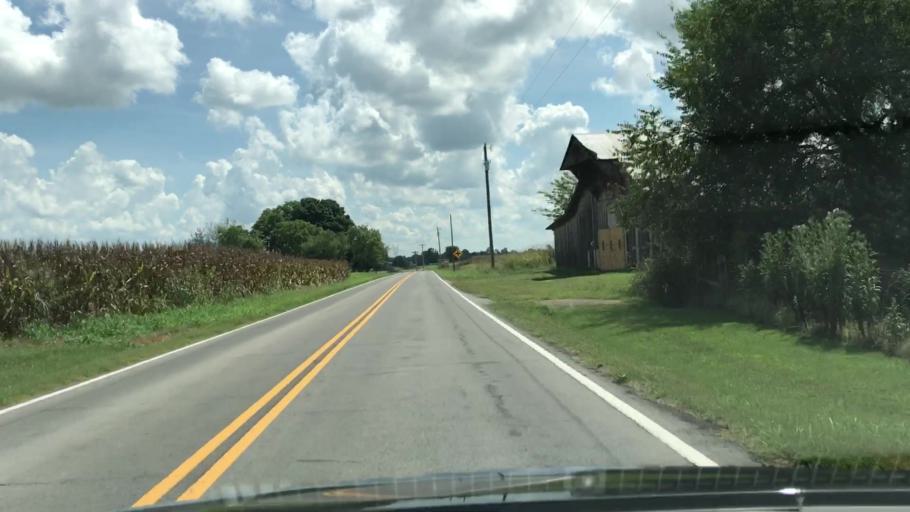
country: US
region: Tennessee
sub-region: Robertson County
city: Springfield
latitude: 36.5833
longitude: -86.8815
